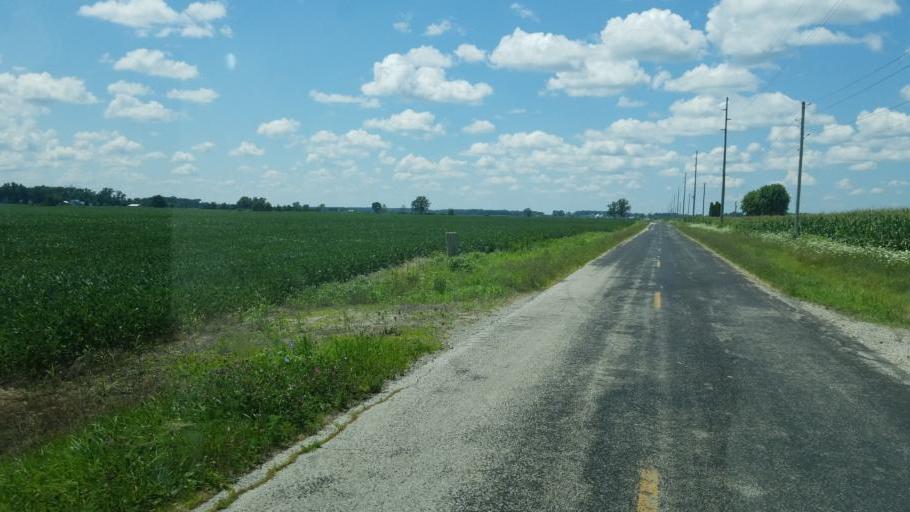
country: US
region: Ohio
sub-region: Marion County
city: Marion
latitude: 40.6884
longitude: -83.1016
